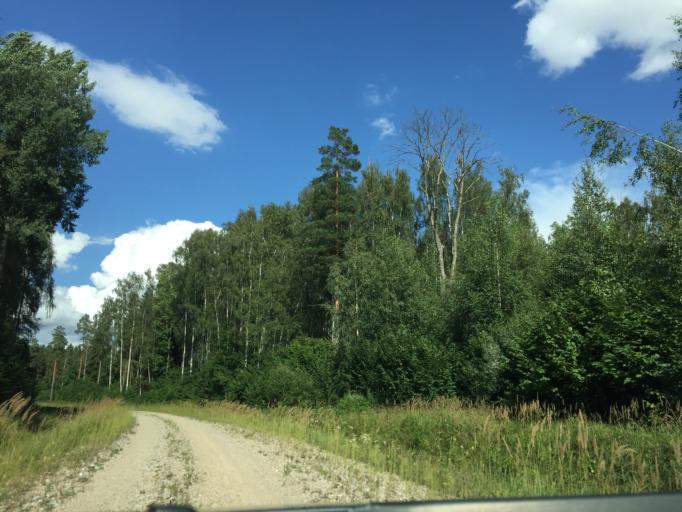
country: LT
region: Siauliu apskritis
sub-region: Joniskis
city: Joniskis
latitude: 56.3528
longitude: 23.5850
